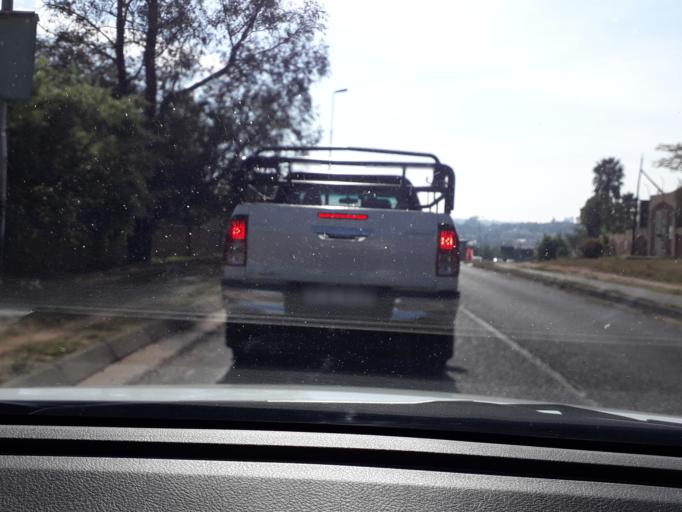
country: ZA
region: Gauteng
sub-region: City of Johannesburg Metropolitan Municipality
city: Roodepoort
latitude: -26.0776
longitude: 27.9666
